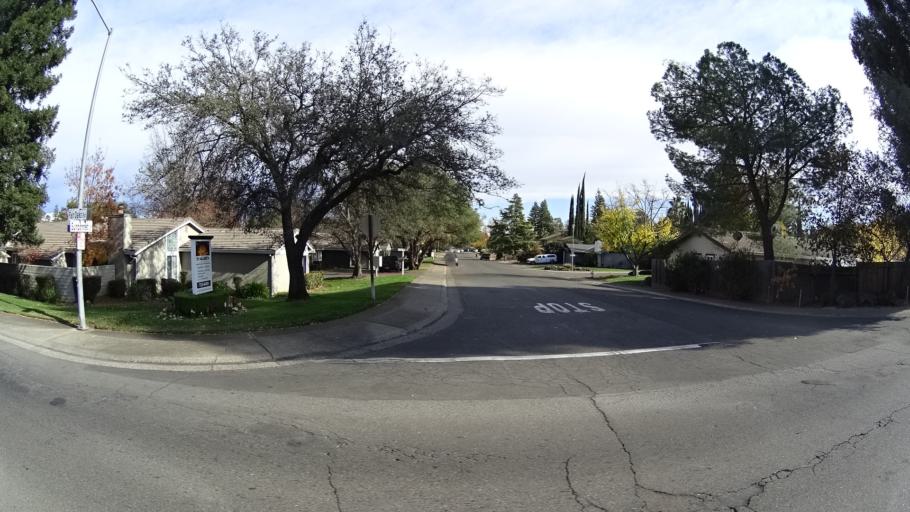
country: US
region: California
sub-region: Sacramento County
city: Fair Oaks
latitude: 38.6754
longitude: -121.2621
